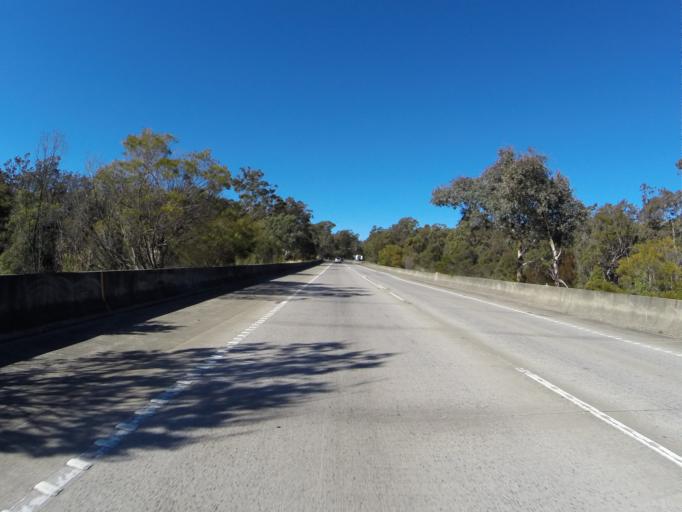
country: AU
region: New South Wales
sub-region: Wollondilly
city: Douglas Park
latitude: -34.2472
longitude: 150.7014
